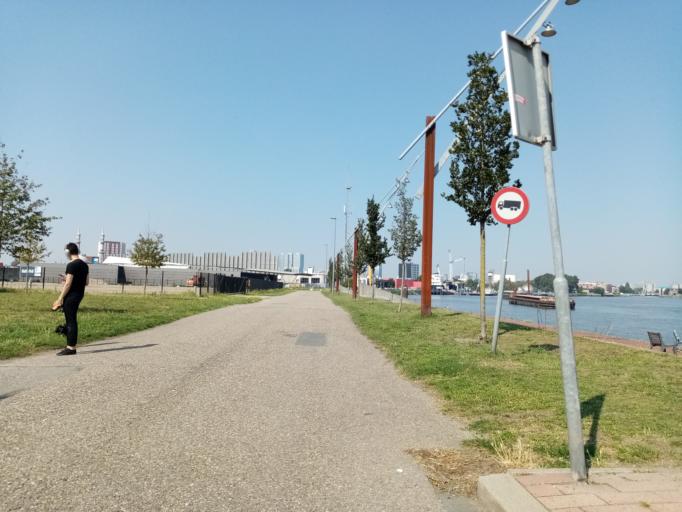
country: NL
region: South Holland
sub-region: Gemeente Rotterdam
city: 's-Gravenland
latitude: 51.8985
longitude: 4.5209
